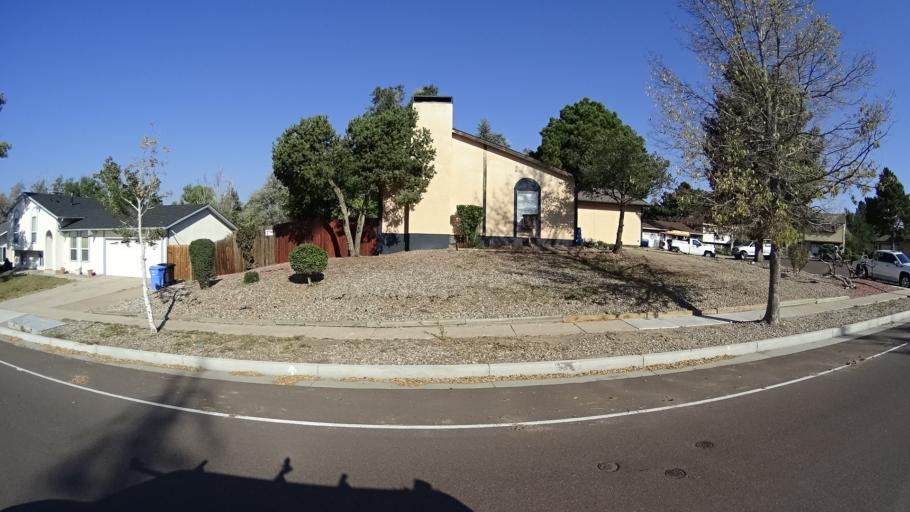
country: US
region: Colorado
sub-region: El Paso County
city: Cimarron Hills
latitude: 38.8774
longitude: -104.7369
